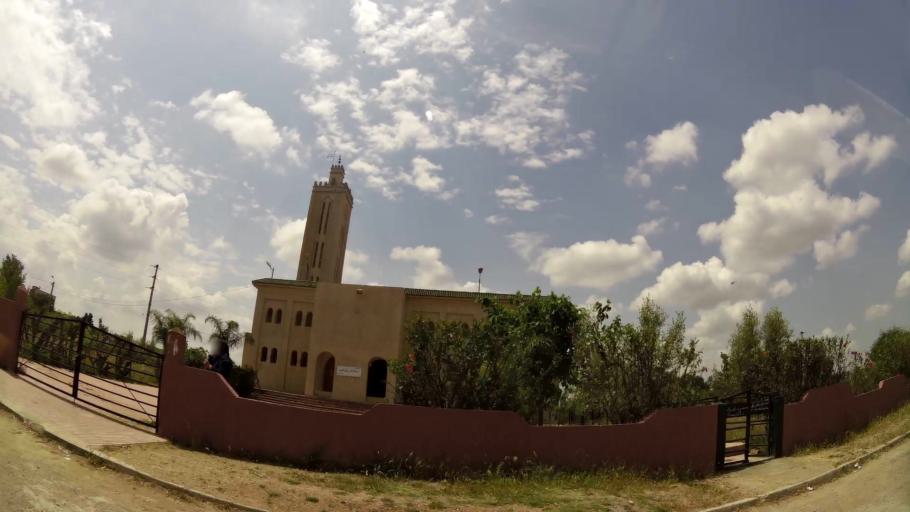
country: MA
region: Gharb-Chrarda-Beni Hssen
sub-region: Kenitra Province
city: Kenitra
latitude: 34.0083
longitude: -6.5387
